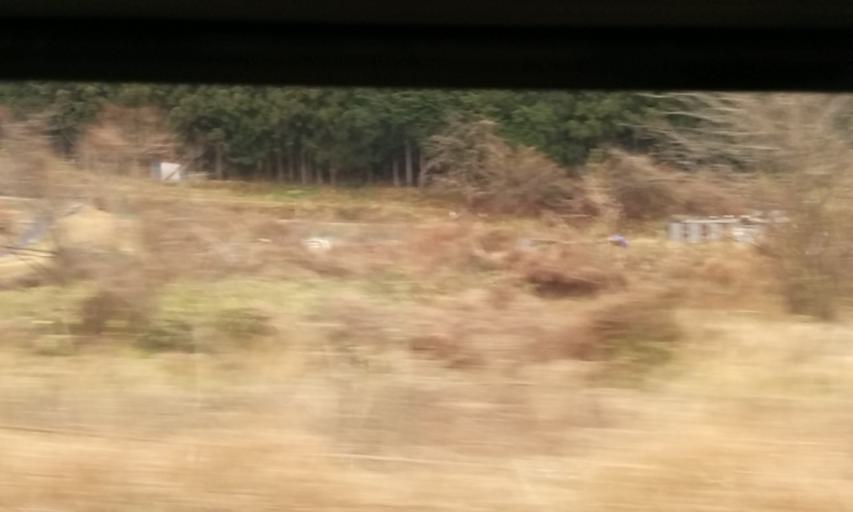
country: JP
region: Nagano
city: Ina
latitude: 35.7563
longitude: 137.7100
